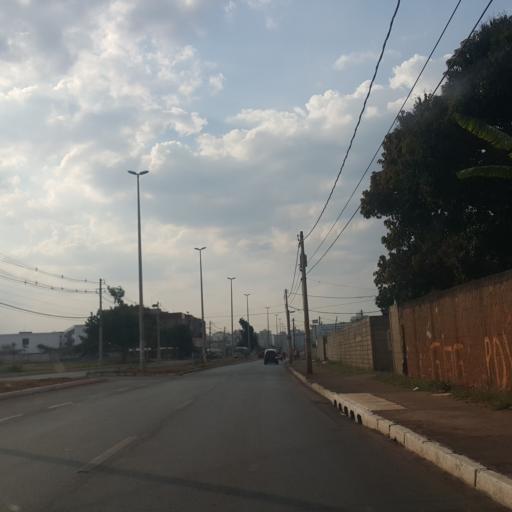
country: BR
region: Federal District
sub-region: Brasilia
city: Brasilia
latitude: -15.8559
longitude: -48.0304
